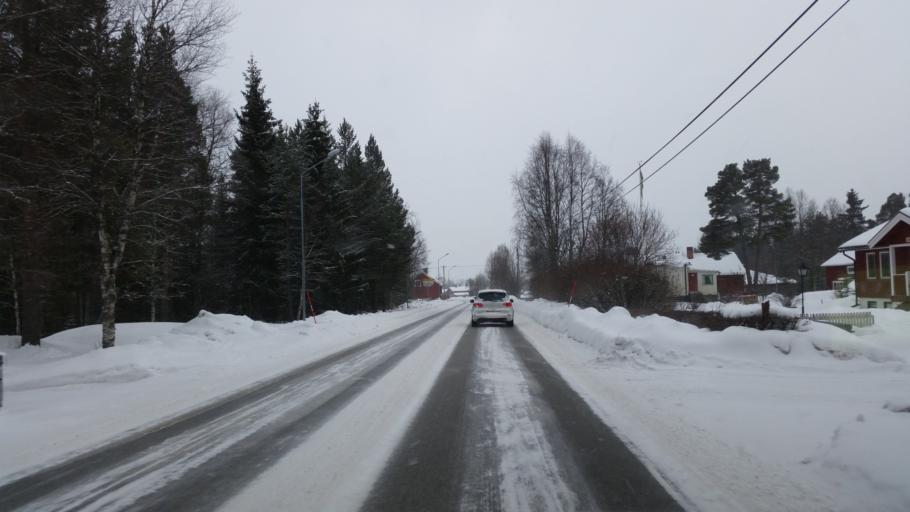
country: SE
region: Jaemtland
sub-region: Harjedalens Kommun
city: Sveg
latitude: 62.4562
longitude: 13.8633
